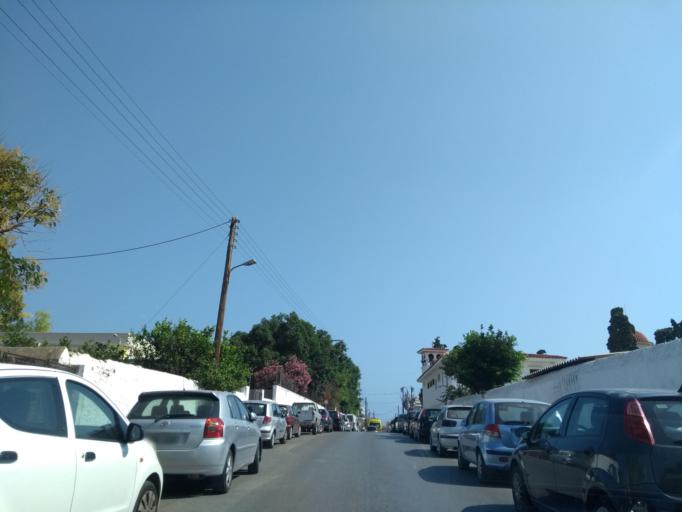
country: GR
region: Crete
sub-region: Nomos Chanias
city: Chania
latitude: 35.5067
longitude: 24.0197
